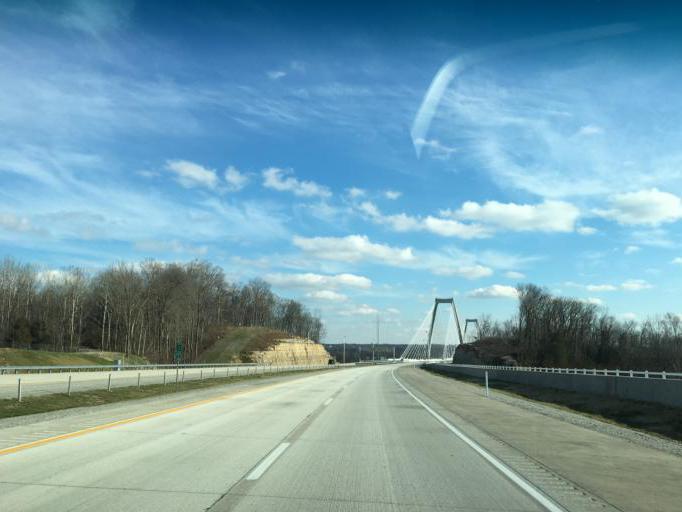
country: US
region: Kentucky
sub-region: Jefferson County
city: Prospect
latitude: 38.3473
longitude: -85.6498
